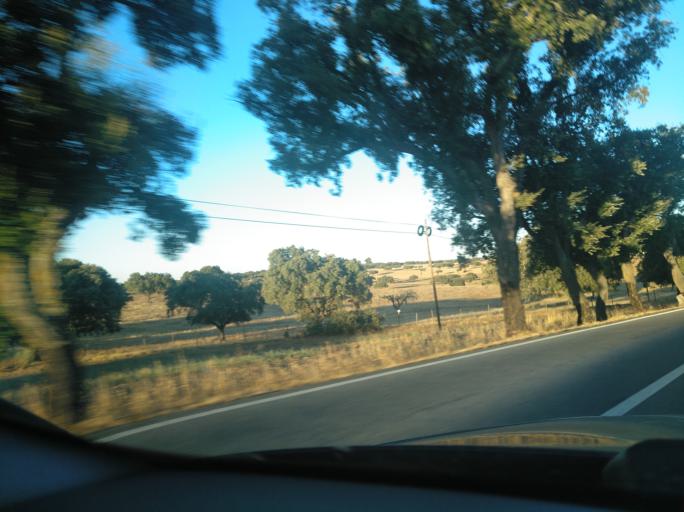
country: PT
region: Portalegre
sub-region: Campo Maior
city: Campo Maior
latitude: 39.0645
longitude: -7.1317
